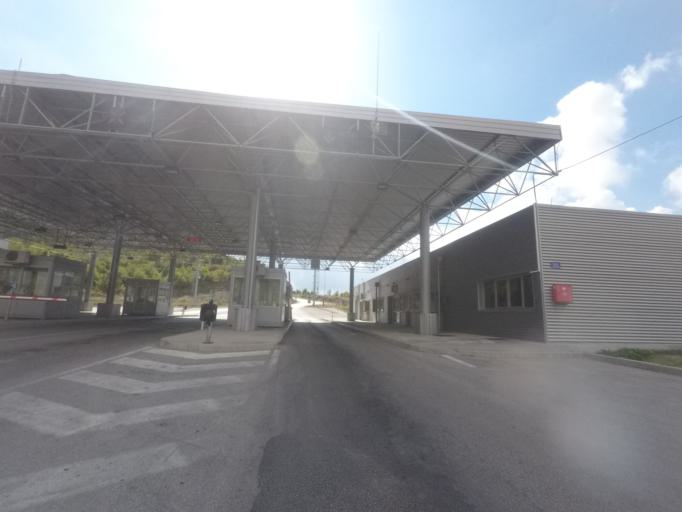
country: ME
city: Igalo
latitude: 42.5820
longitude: 18.4306
